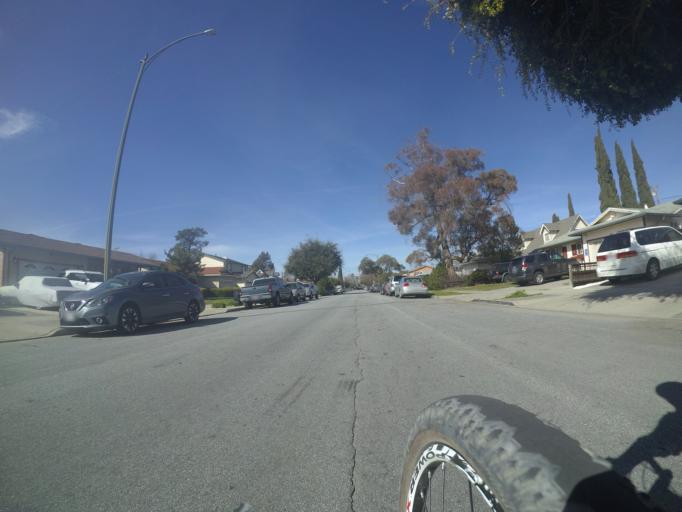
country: US
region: California
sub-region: Santa Clara County
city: Milpitas
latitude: 37.4177
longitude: -121.8666
